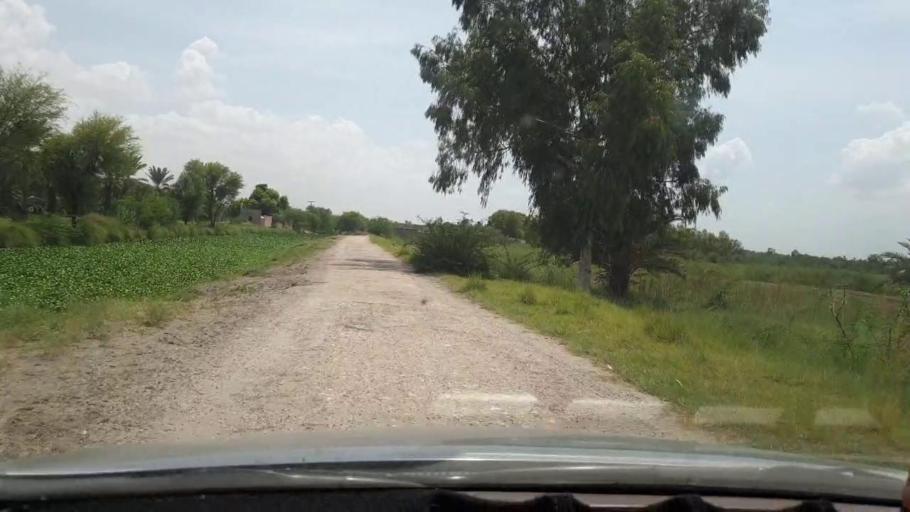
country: PK
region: Sindh
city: Khairpur
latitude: 27.4686
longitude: 68.7968
